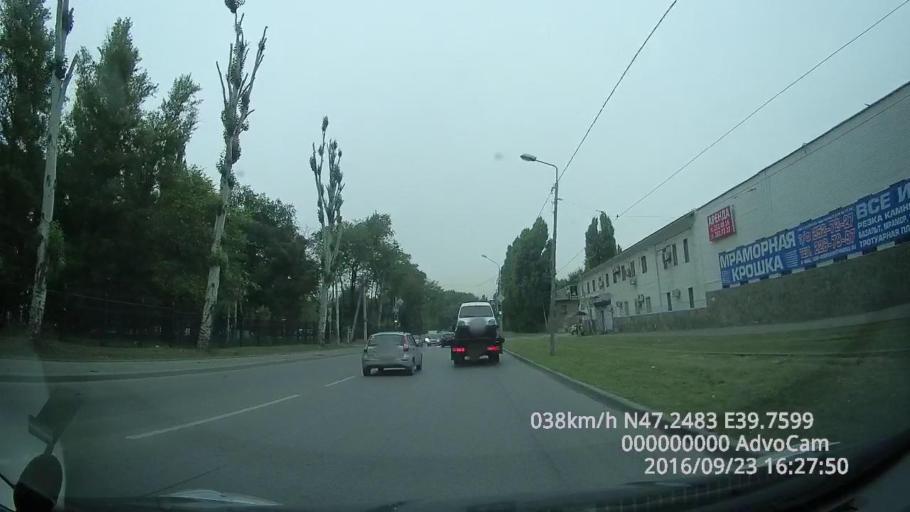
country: RU
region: Rostov
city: Imeni Chkalova
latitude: 47.2482
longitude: 39.7599
